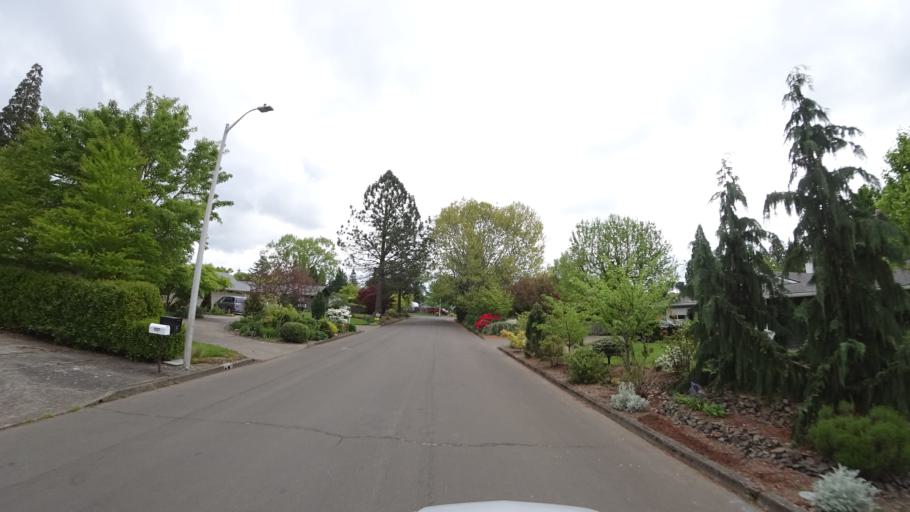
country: US
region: Oregon
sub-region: Washington County
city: Hillsboro
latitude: 45.5310
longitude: -122.9742
